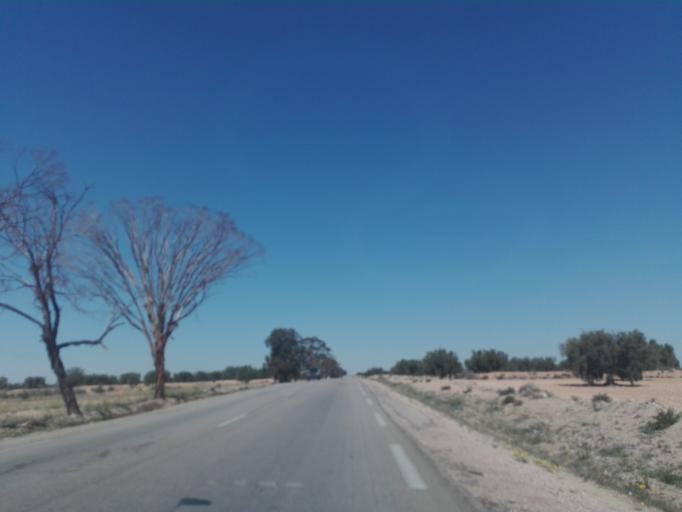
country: TN
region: Safaqis
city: Bi'r `Ali Bin Khalifah
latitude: 34.7514
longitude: 10.3443
